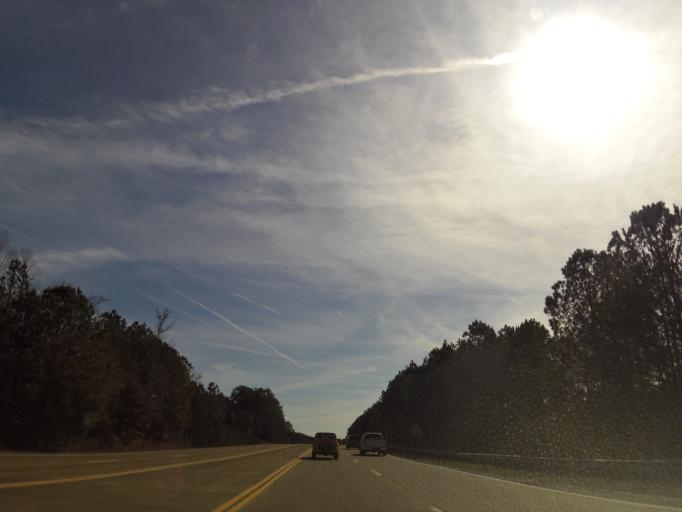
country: US
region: Georgia
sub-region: Whitfield County
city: Dalton
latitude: 34.7827
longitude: -84.9173
